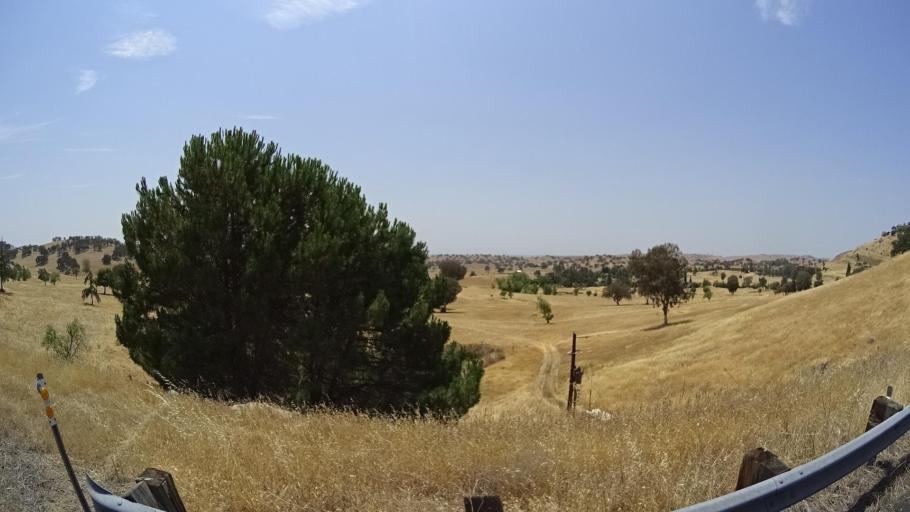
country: US
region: California
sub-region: Tuolumne County
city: Jamestown
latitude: 37.6336
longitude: -120.3464
